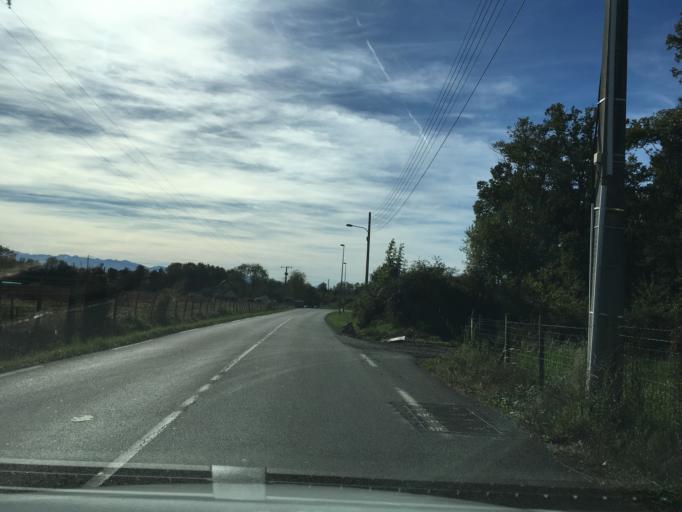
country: FR
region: Aquitaine
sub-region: Departement des Pyrenees-Atlantiques
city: Montardon
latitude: 43.3313
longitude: -0.3356
